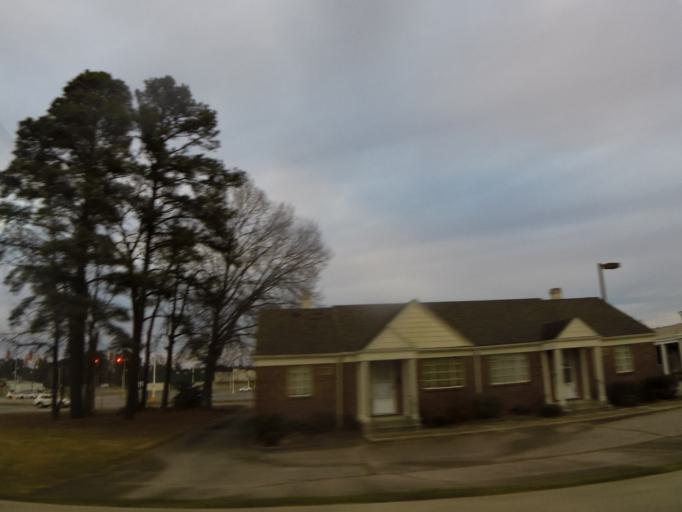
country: US
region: North Carolina
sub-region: Nash County
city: Rocky Mount
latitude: 35.9559
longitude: -77.8223
